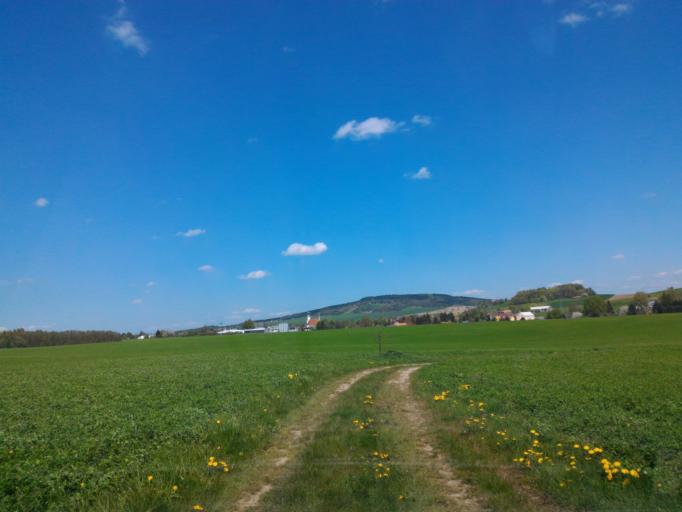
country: DE
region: Saxony
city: Eibau
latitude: 50.9693
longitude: 14.6693
